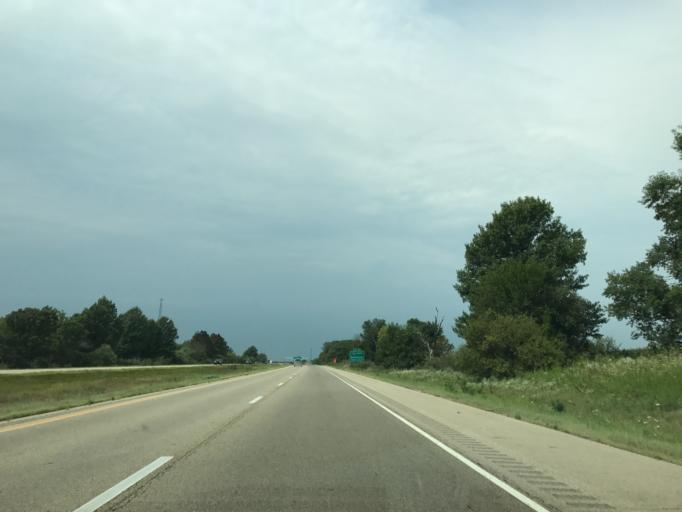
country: US
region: Illinois
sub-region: Bureau County
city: Depue
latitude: 41.4001
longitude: -89.3647
